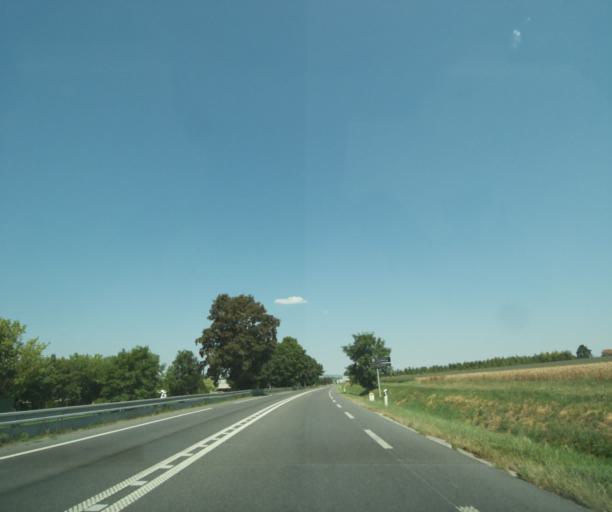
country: FR
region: Champagne-Ardenne
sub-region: Departement de la Marne
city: Verzy
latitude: 49.1332
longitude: 4.2326
